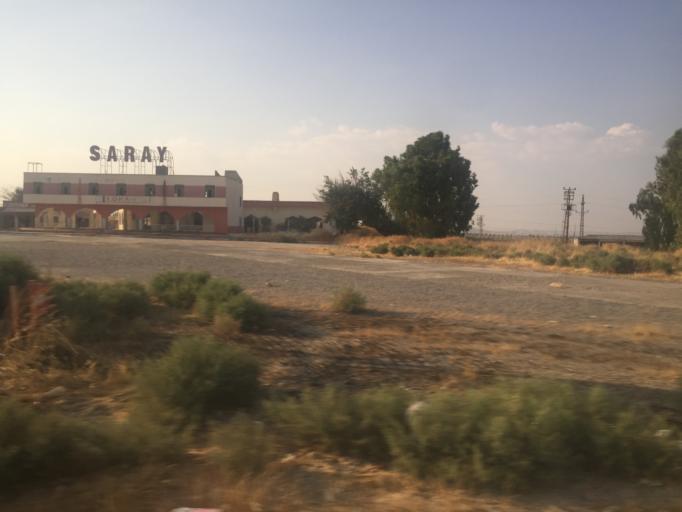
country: TR
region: Sanliurfa
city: Birecik
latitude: 37.0235
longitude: 37.9210
